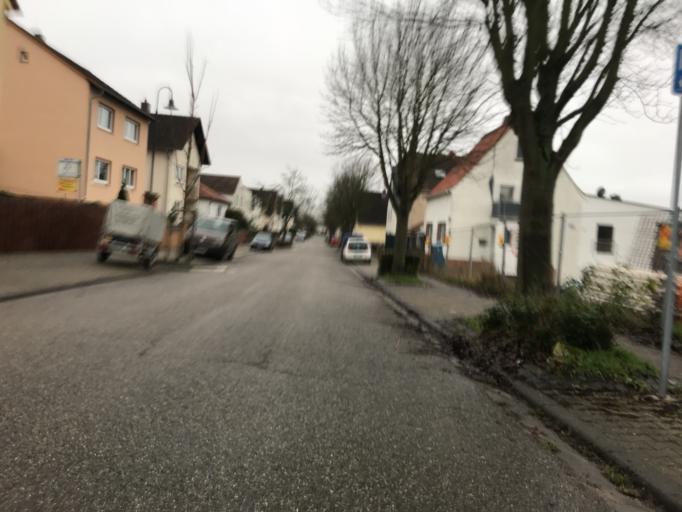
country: DE
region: Rheinland-Pfalz
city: Sorgenloch
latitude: 49.8800
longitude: 8.2009
